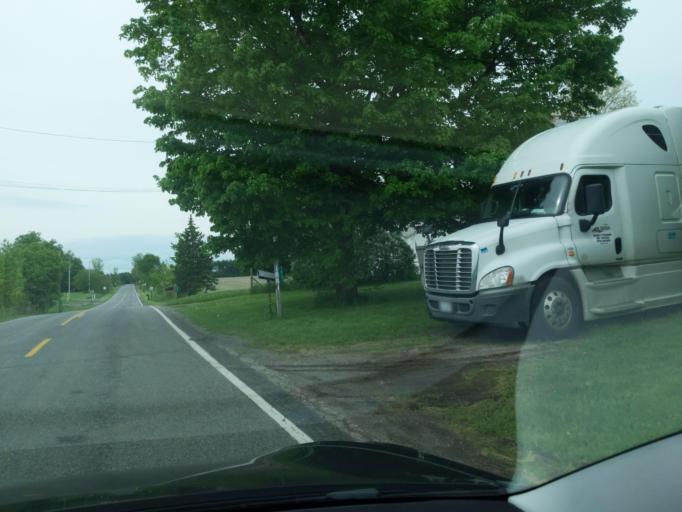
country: US
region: Michigan
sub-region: Ingham County
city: Mason
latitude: 42.5274
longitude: -84.4281
